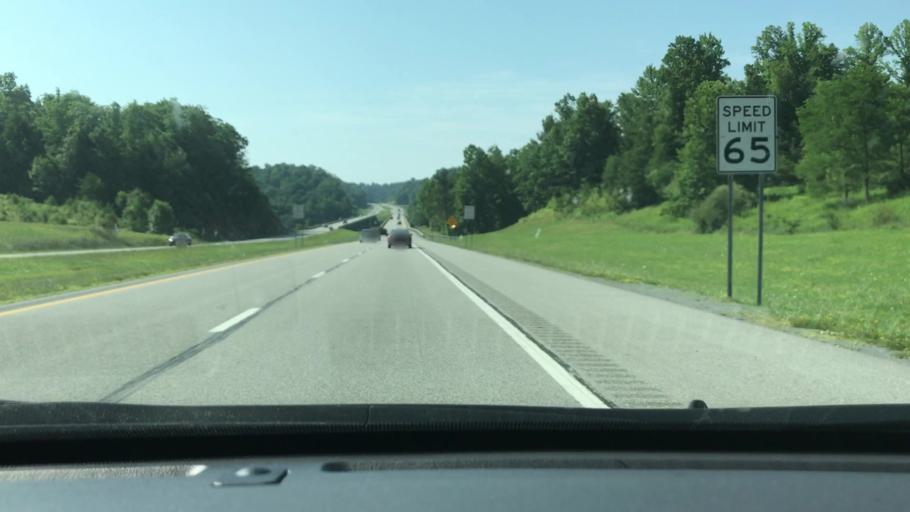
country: US
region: West Virginia
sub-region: Nicholas County
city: Summersville
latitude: 38.2448
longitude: -80.8566
